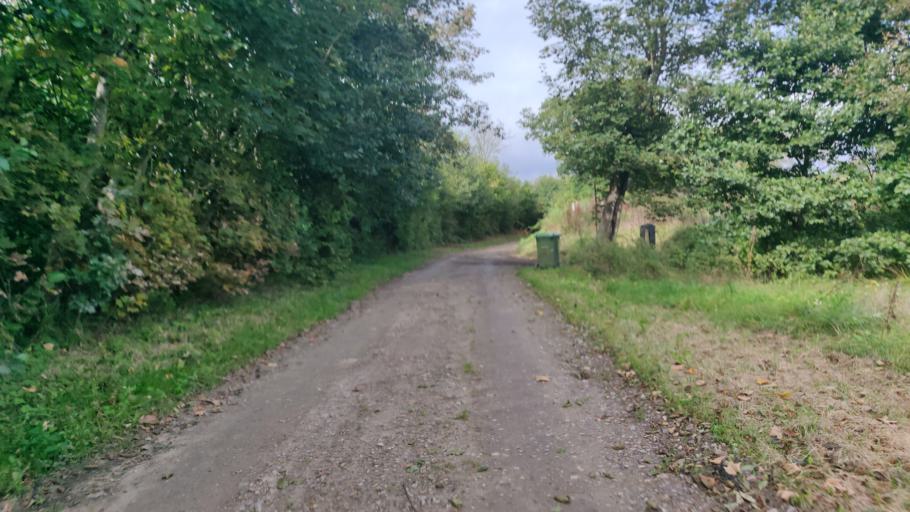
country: DK
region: South Denmark
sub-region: Kolding Kommune
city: Lunderskov
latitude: 55.5491
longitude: 9.3498
